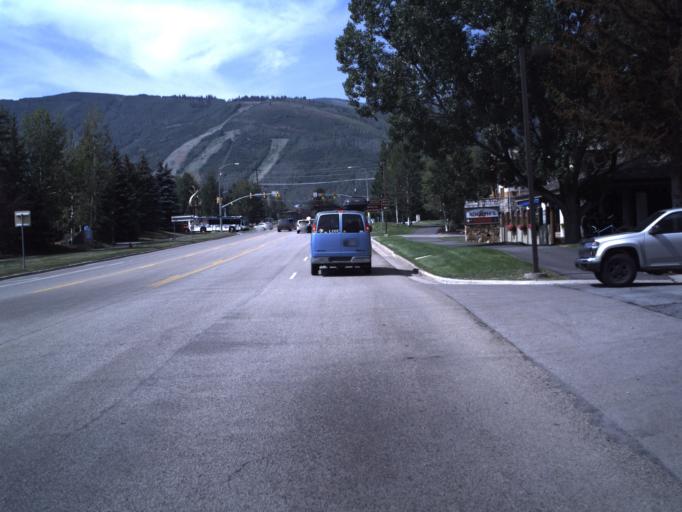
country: US
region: Utah
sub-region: Summit County
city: Park City
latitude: 40.6641
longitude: -111.4994
